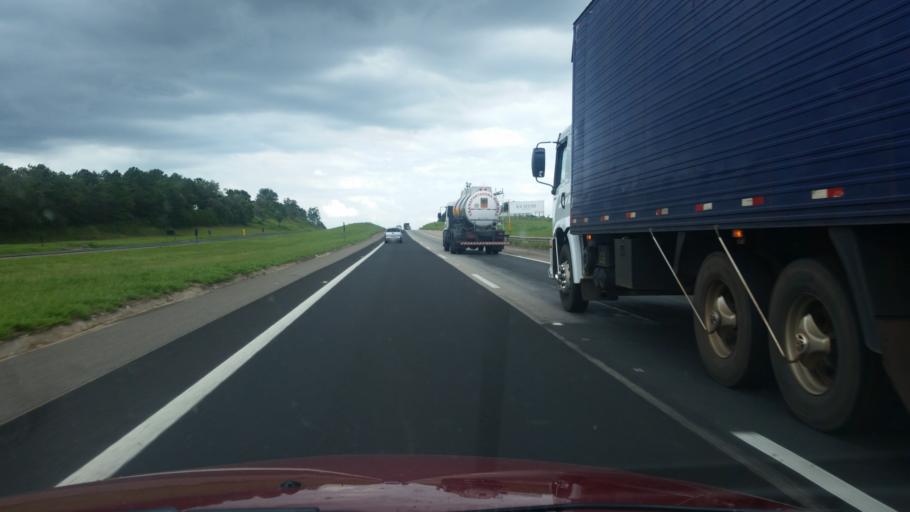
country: BR
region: Sao Paulo
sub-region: Sorocaba
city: Sorocaba
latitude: -23.3830
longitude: -47.3902
